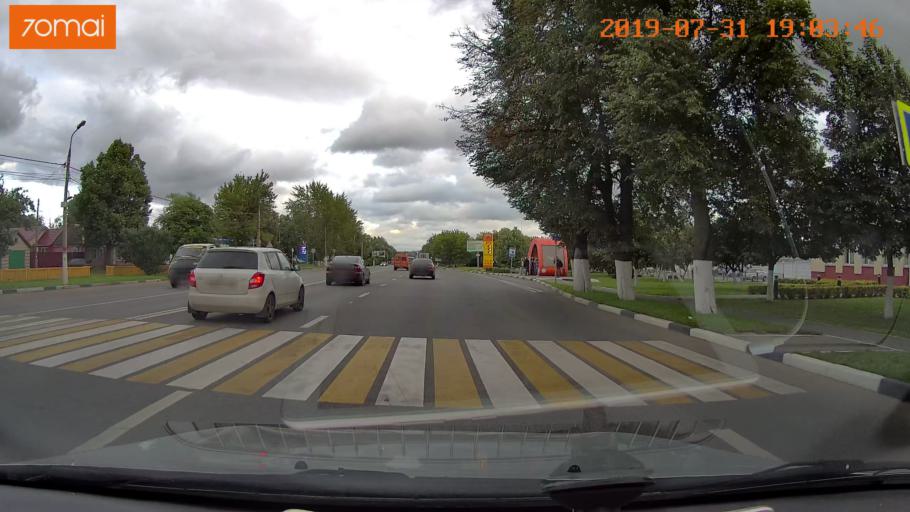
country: RU
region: Moskovskaya
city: Raduzhnyy
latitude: 55.1130
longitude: 38.7381
